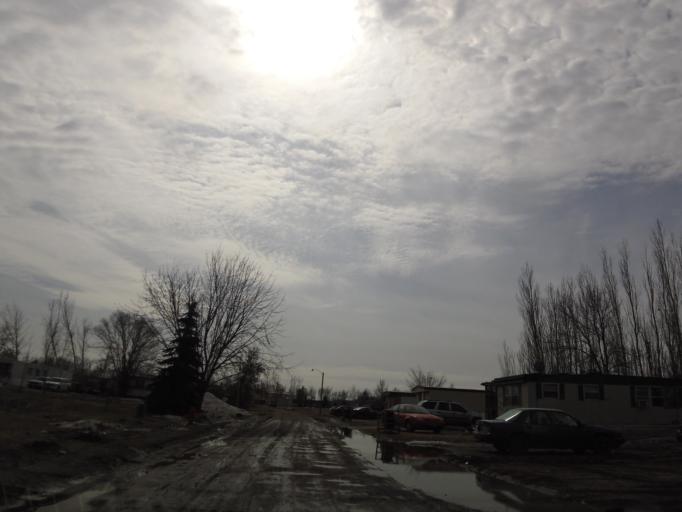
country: US
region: North Dakota
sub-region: Walsh County
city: Grafton
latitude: 48.2950
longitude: -97.3815
